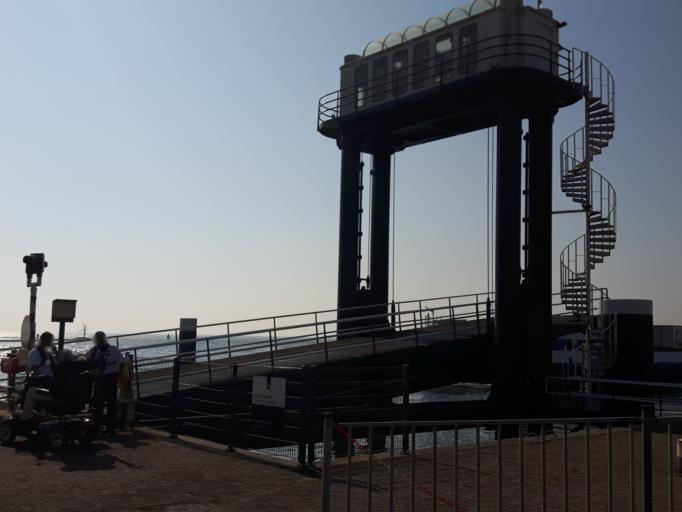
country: NL
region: Friesland
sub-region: Gemeente Terschelling
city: West-Terschelling
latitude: 53.3570
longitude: 5.2171
